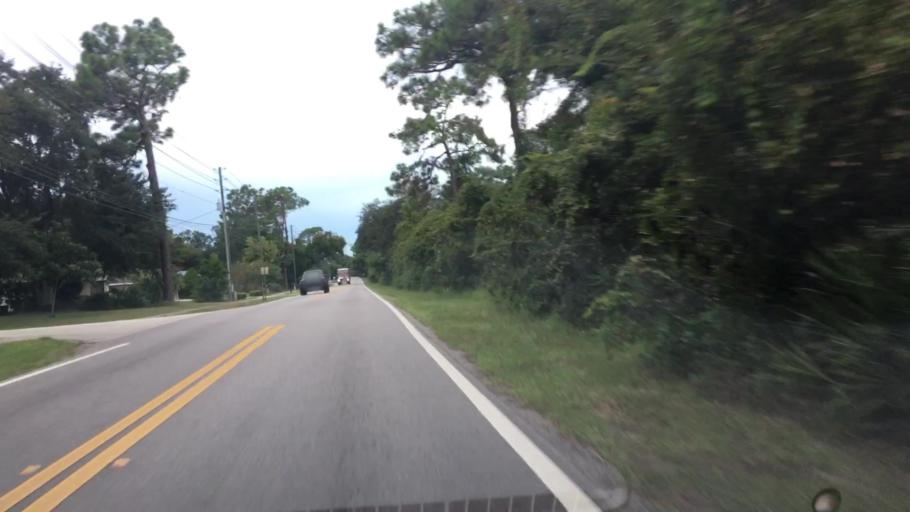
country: US
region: Florida
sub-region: Volusia County
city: DeBary
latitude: 28.8902
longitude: -81.2964
